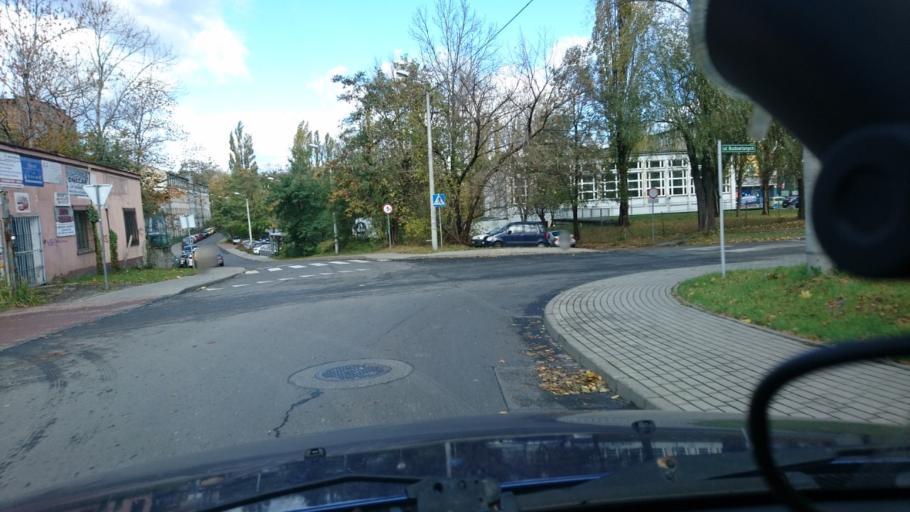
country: PL
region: Silesian Voivodeship
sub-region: Bielsko-Biala
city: Bielsko-Biala
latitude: 49.8321
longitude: 19.0412
